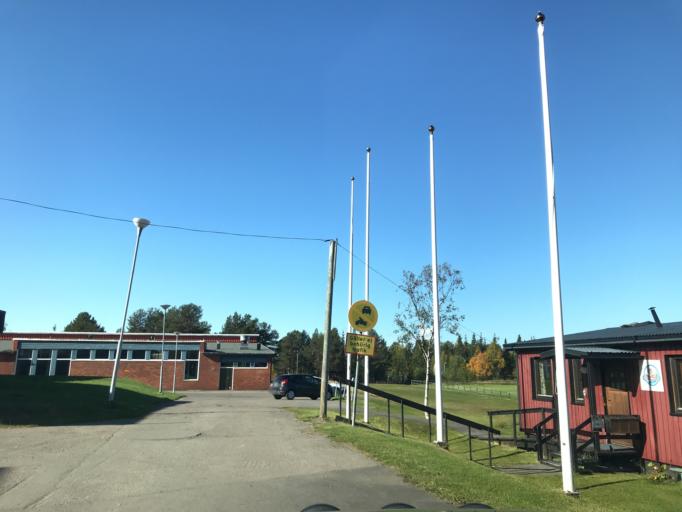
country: SE
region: Norrbotten
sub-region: Gallivare Kommun
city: Malmberget
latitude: 67.6498
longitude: 21.0552
